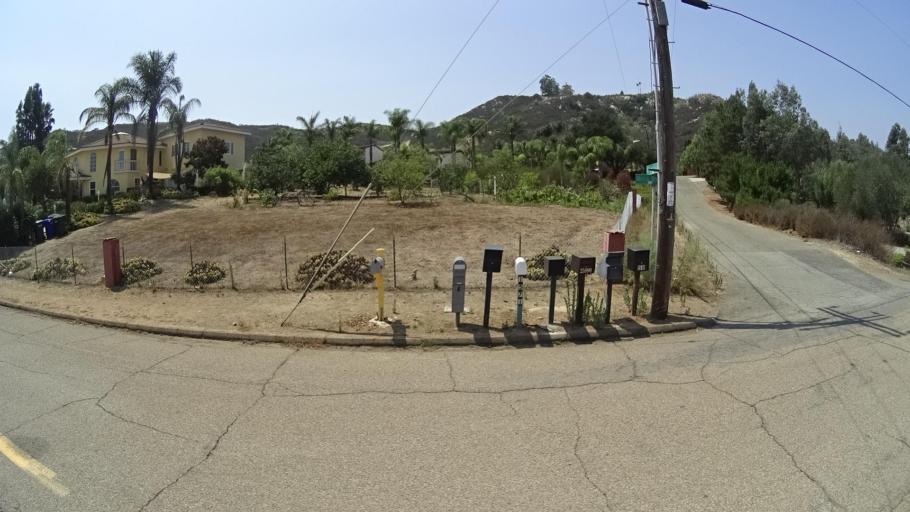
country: US
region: California
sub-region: San Diego County
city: Hidden Meadows
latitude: 33.1829
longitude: -117.1184
